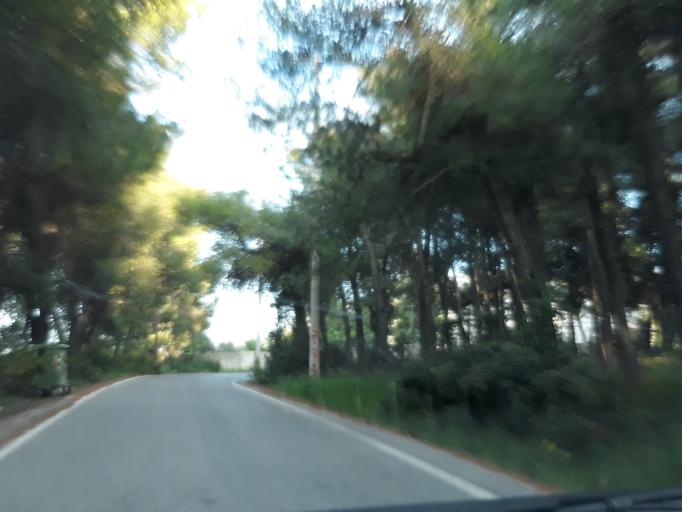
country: GR
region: Attica
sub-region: Nomarchia Anatolikis Attikis
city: Afidnes
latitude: 38.2338
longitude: 23.7877
